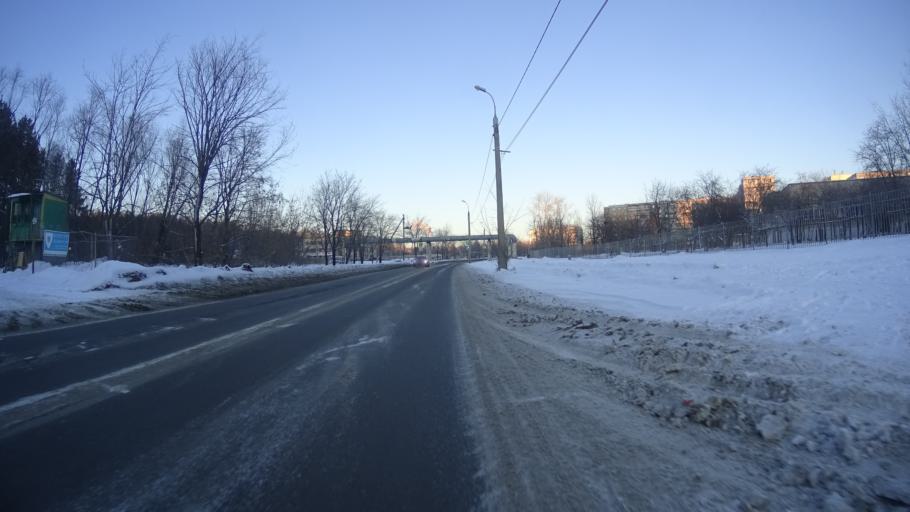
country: RU
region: Chelyabinsk
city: Roshchino
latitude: 55.1977
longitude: 61.3003
